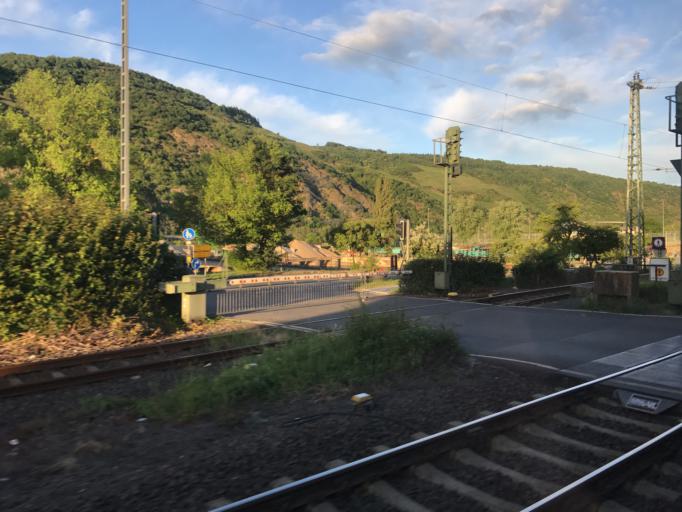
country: DE
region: Rheinland-Pfalz
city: Oberwesel
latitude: 50.1048
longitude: 7.7310
